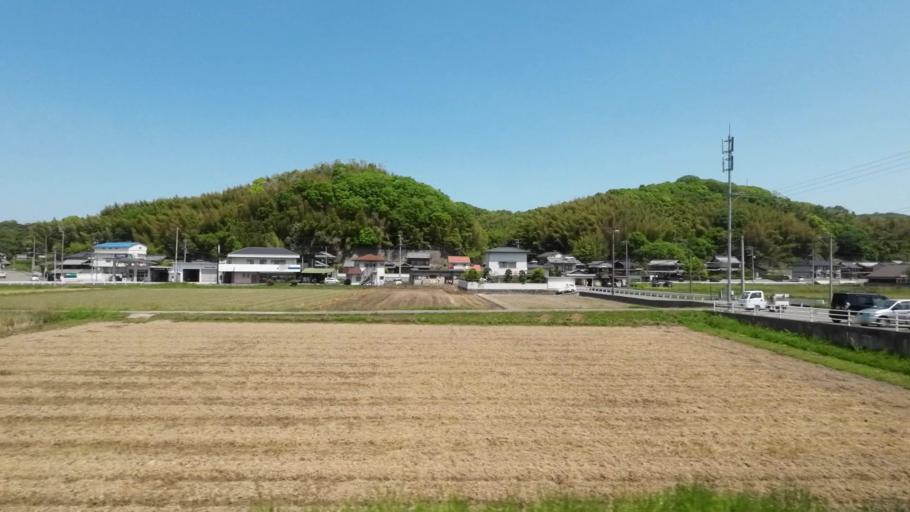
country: JP
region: Ehime
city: Hojo
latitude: 34.0952
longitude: 132.9426
